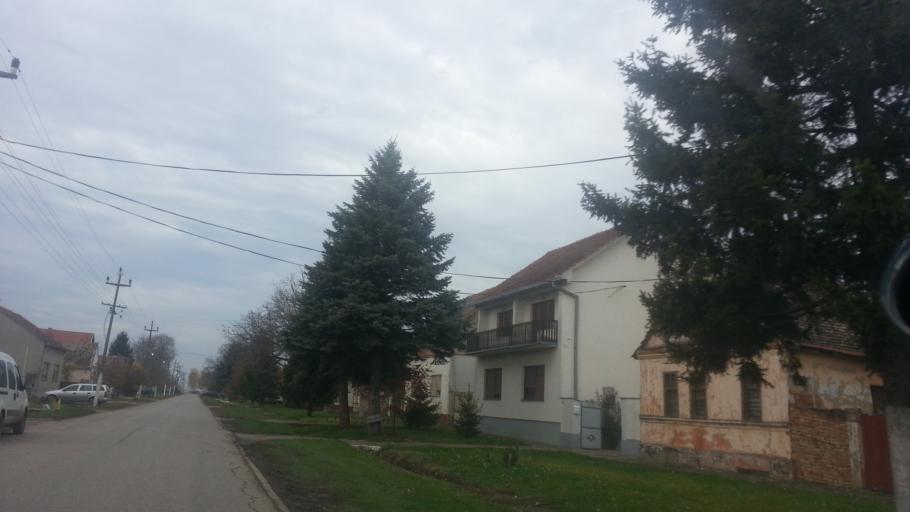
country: RS
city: Golubinci
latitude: 44.9940
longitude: 20.0614
